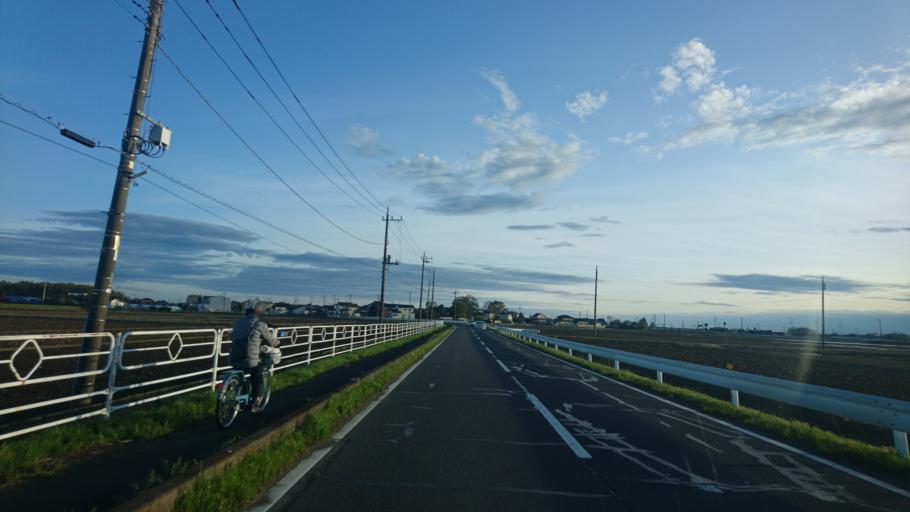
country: JP
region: Ibaraki
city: Ishige
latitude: 36.1552
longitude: 139.9970
